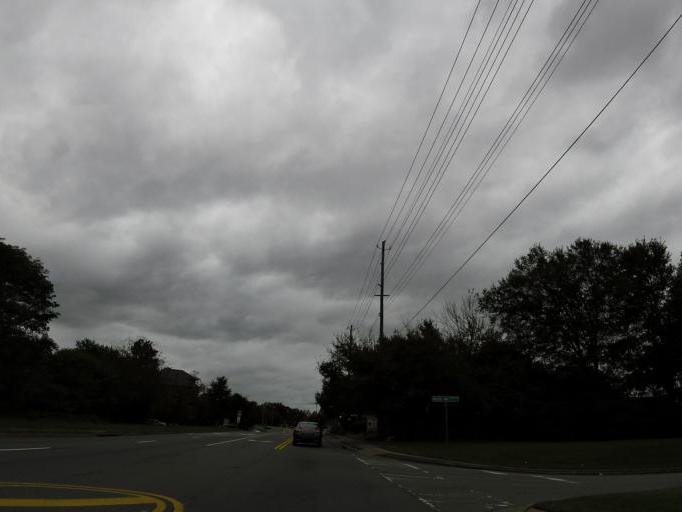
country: US
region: Georgia
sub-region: Cobb County
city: Marietta
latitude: 33.9751
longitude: -84.5532
